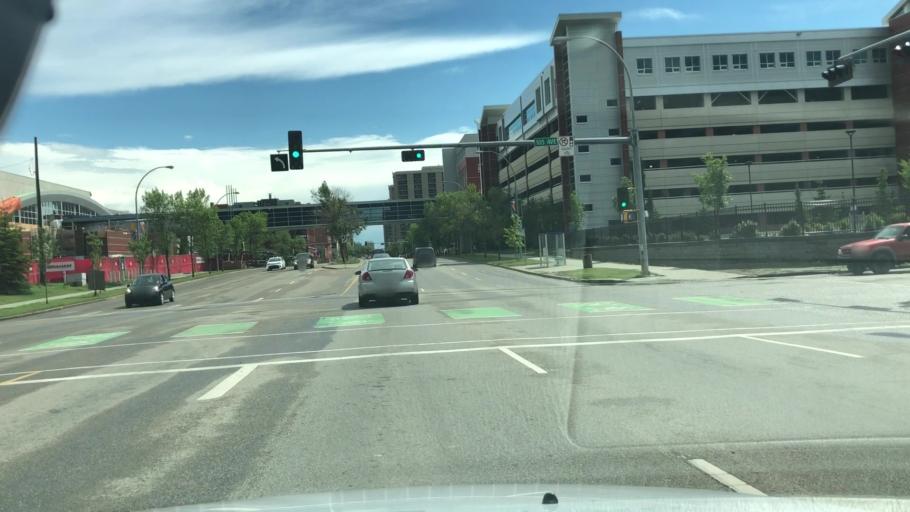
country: CA
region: Alberta
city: Edmonton
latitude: 53.5485
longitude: -113.5085
